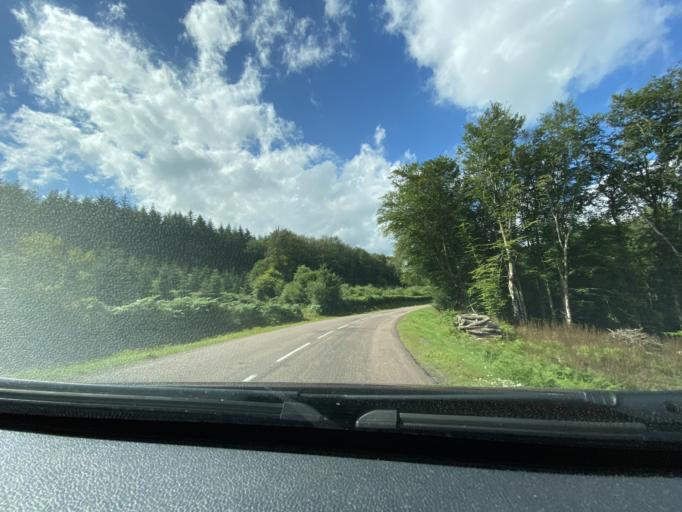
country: FR
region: Bourgogne
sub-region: Departement de la Cote-d'Or
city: Saulieu
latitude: 47.2637
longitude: 4.1242
